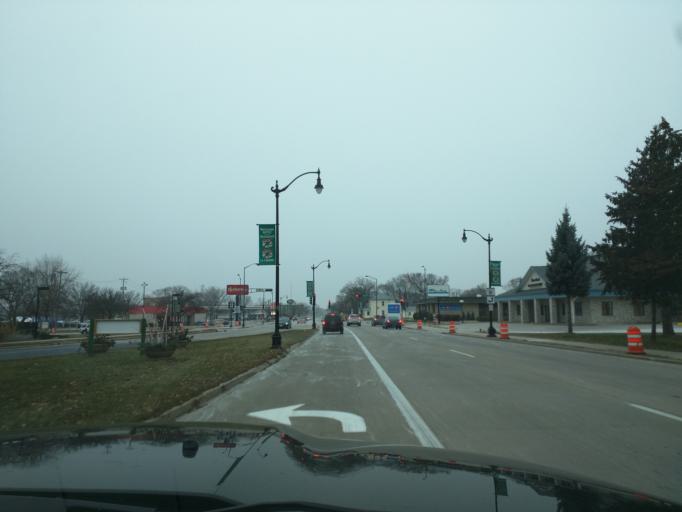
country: US
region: Wisconsin
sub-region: La Crosse County
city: North La Crosse
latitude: 43.8404
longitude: -91.2482
